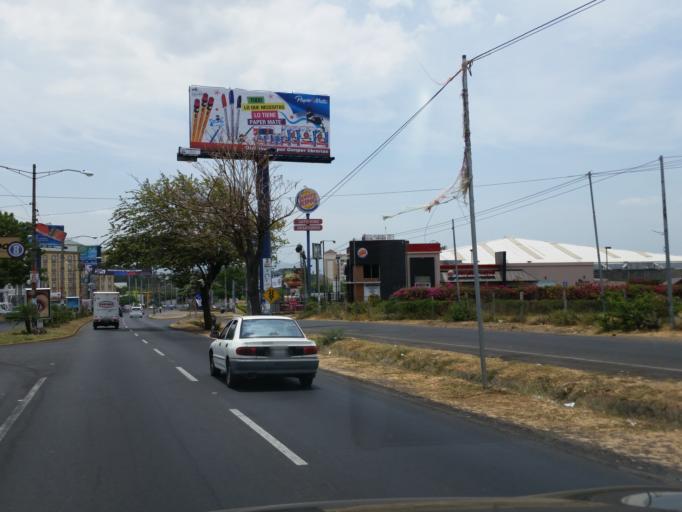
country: NI
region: Managua
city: Managua
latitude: 12.1217
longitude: -86.2628
